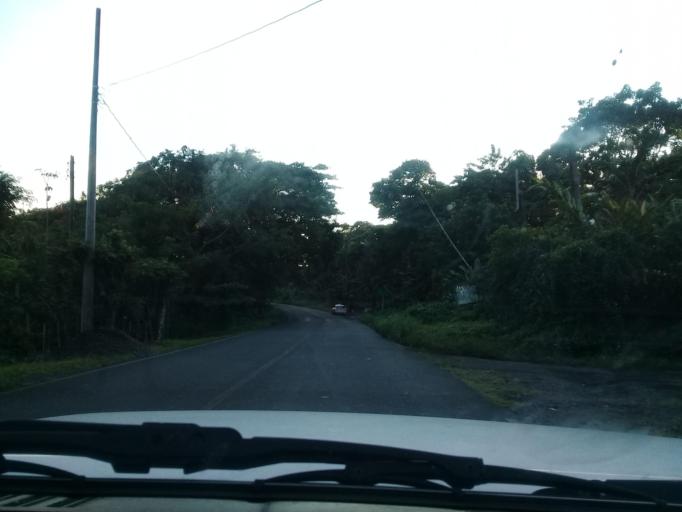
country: MX
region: Veracruz
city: Catemaco
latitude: 18.4301
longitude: -95.0922
